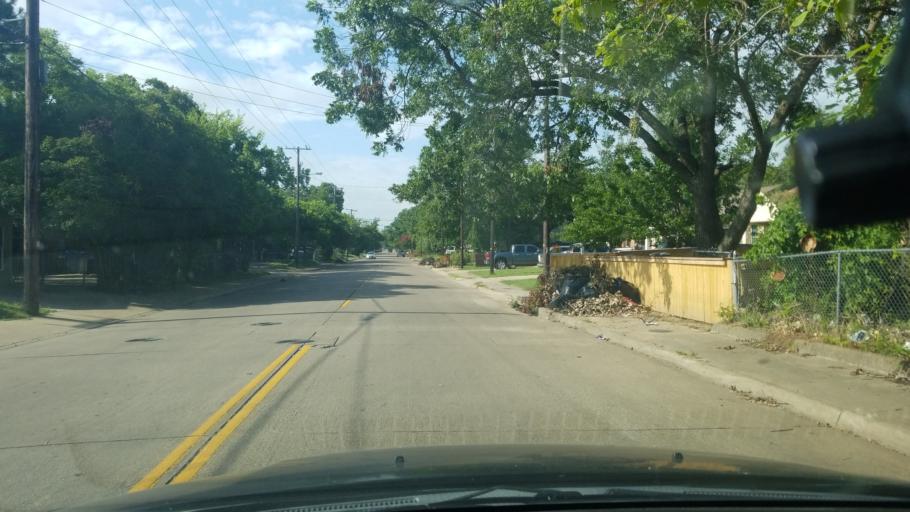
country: US
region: Texas
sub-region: Dallas County
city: Balch Springs
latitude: 32.7338
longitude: -96.6786
